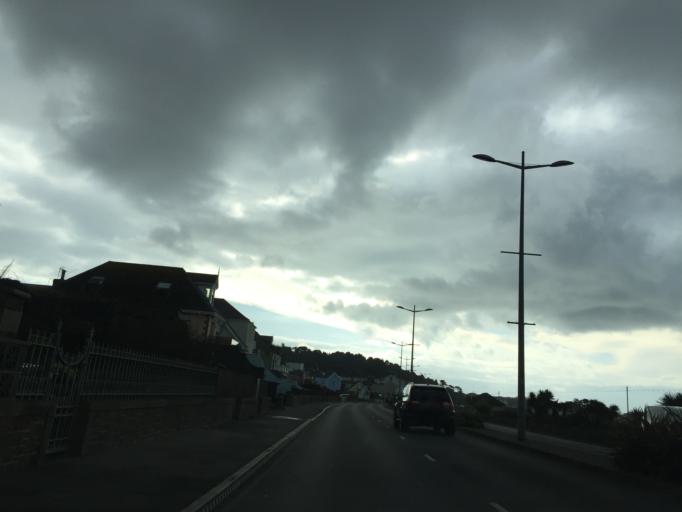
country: JE
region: St Helier
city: Saint Helier
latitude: 49.1949
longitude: -2.1307
